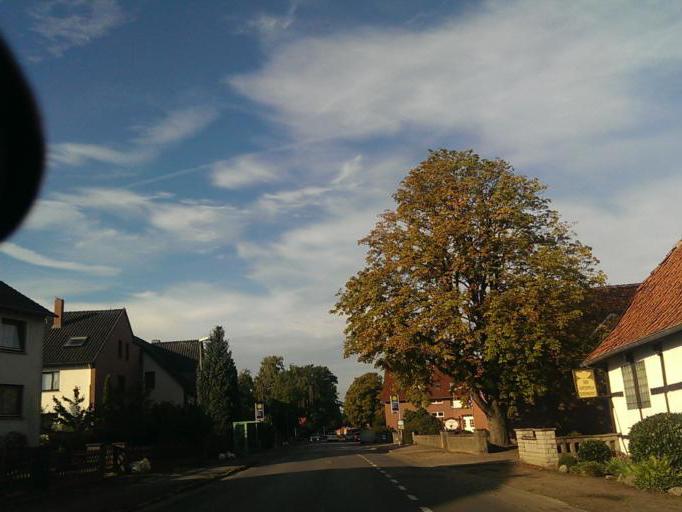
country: DE
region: Lower Saxony
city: Garbsen-Mitte
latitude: 52.4615
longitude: 9.5865
